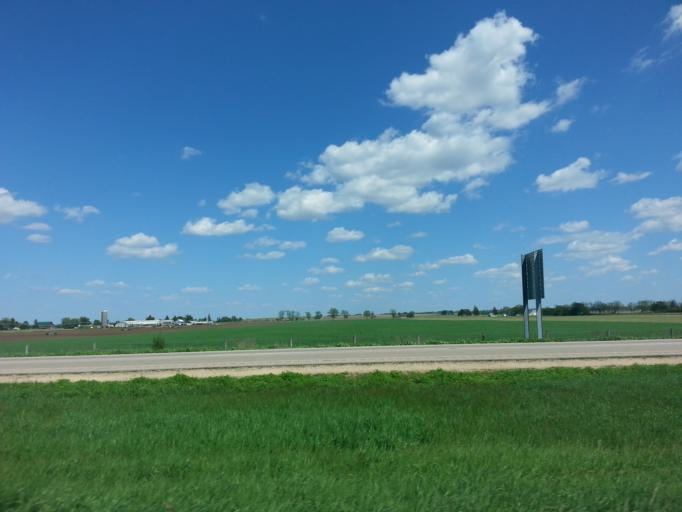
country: US
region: Wisconsin
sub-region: Rock County
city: Janesville
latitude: 42.6484
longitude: -88.9832
